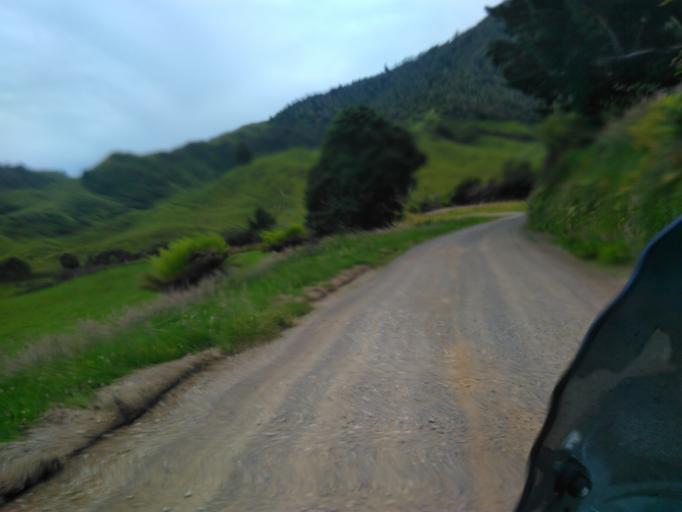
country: NZ
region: Bay of Plenty
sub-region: Opotiki District
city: Opotiki
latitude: -38.1044
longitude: 177.4964
